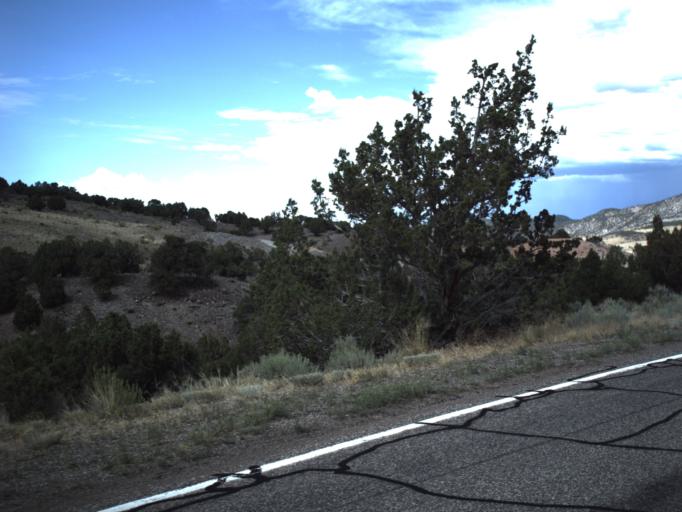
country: US
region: Utah
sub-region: Sevier County
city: Aurora
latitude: 38.7774
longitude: -111.9365
